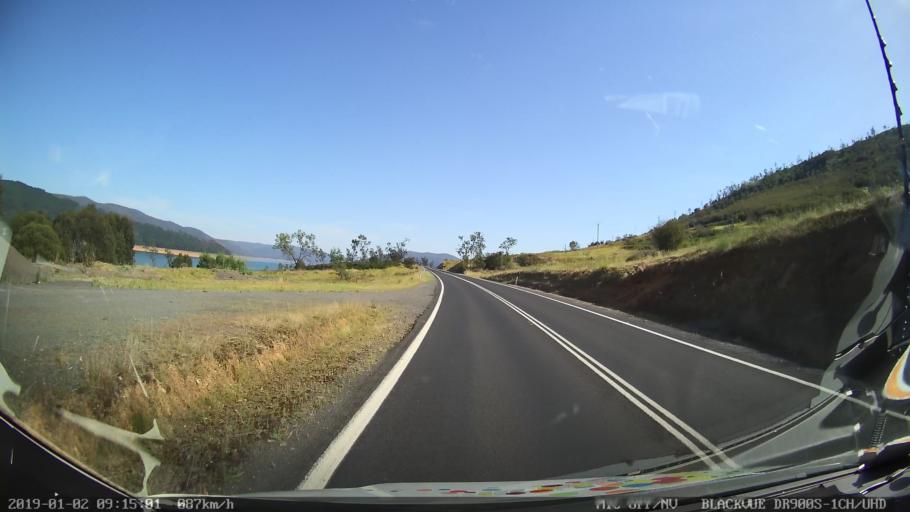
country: AU
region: New South Wales
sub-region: Tumut Shire
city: Tumut
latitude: -35.4704
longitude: 148.2788
